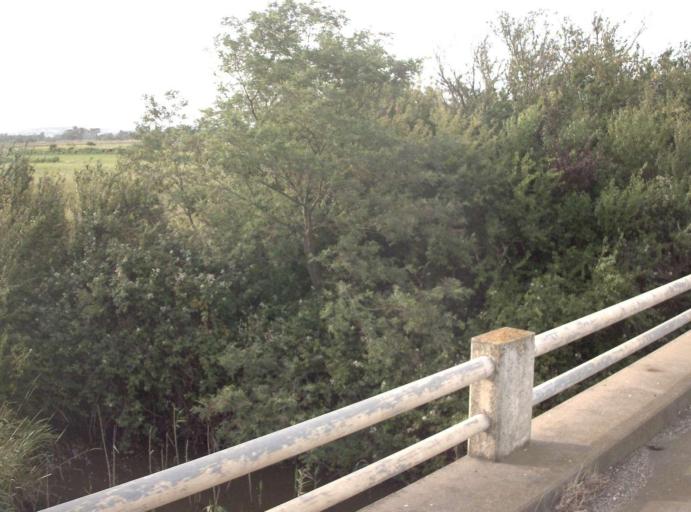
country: AU
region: Victoria
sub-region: Wellington
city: Heyfield
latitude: -37.9744
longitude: 146.8895
